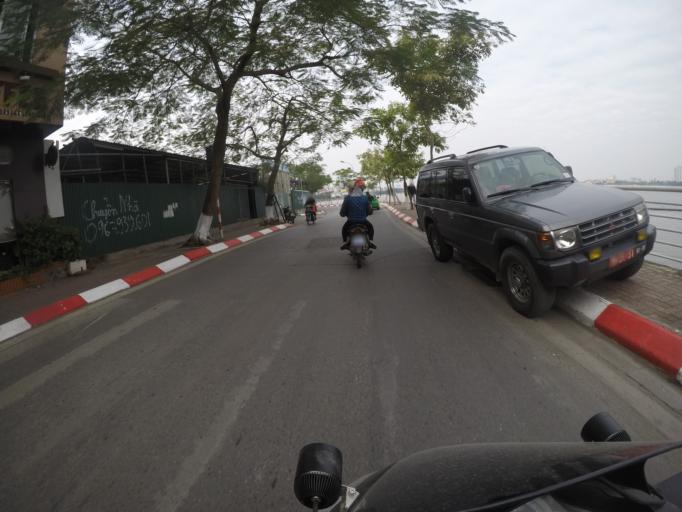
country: VN
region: Ha Noi
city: Tay Ho
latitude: 21.0559
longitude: 105.8103
